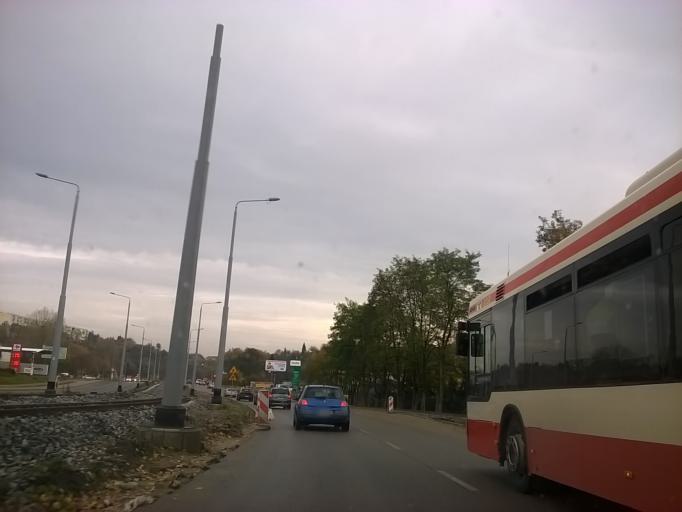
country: PL
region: Pomeranian Voivodeship
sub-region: Powiat gdanski
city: Kowale
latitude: 54.3510
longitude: 18.5932
